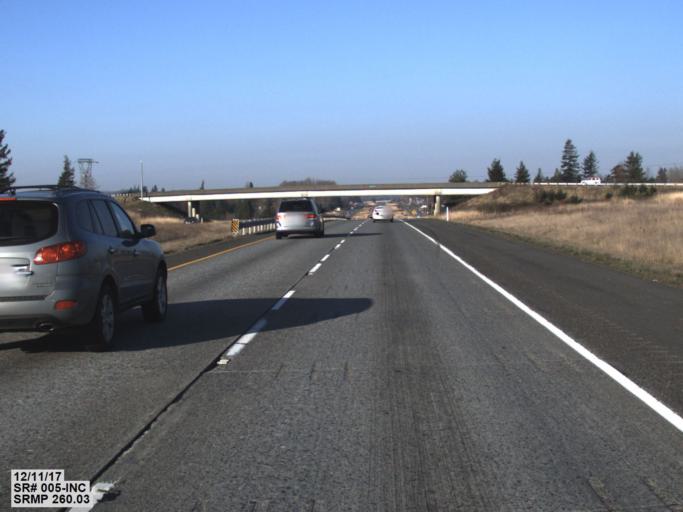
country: US
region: Washington
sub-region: Whatcom County
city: Marietta-Alderwood
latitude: 48.8160
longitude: -122.5468
